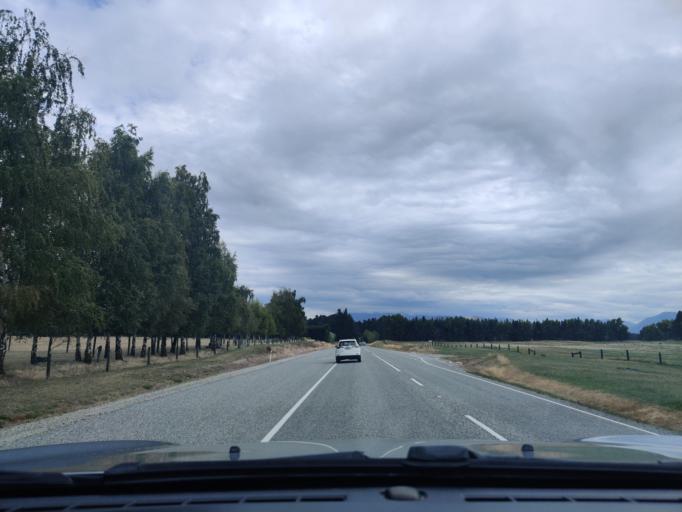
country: NZ
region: Otago
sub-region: Queenstown-Lakes District
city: Wanaka
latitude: -44.7159
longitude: 169.2142
